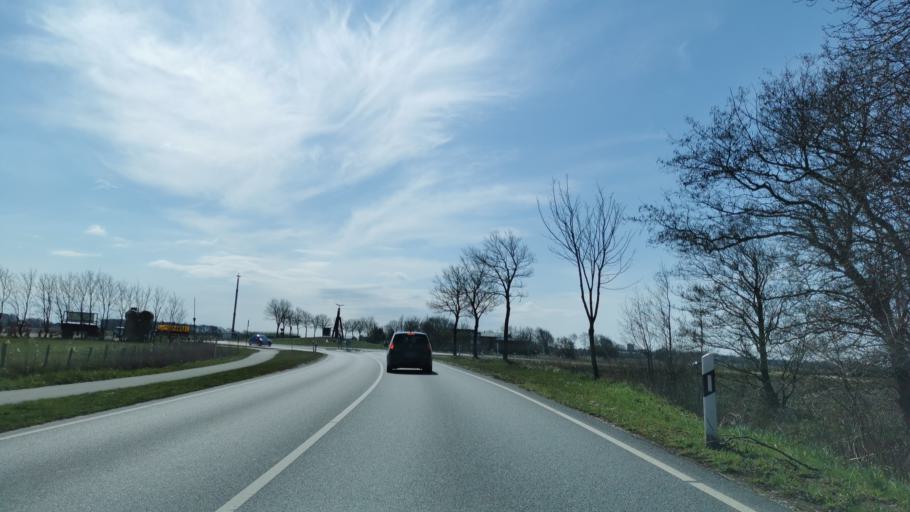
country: DE
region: Schleswig-Holstein
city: Oesterdeichstrich
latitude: 54.1474
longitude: 8.8768
